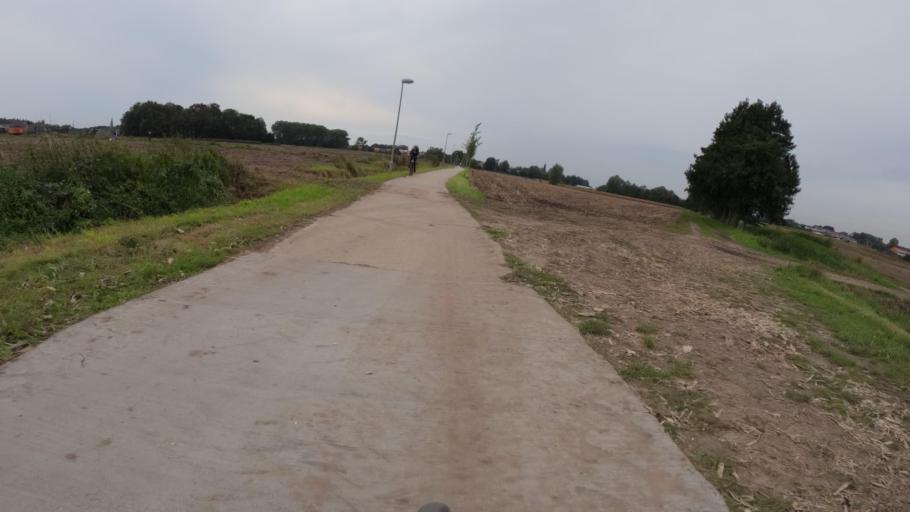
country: BE
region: Flanders
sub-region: Provincie Oost-Vlaanderen
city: Sint-Gillis-Waas
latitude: 51.2162
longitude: 4.0823
